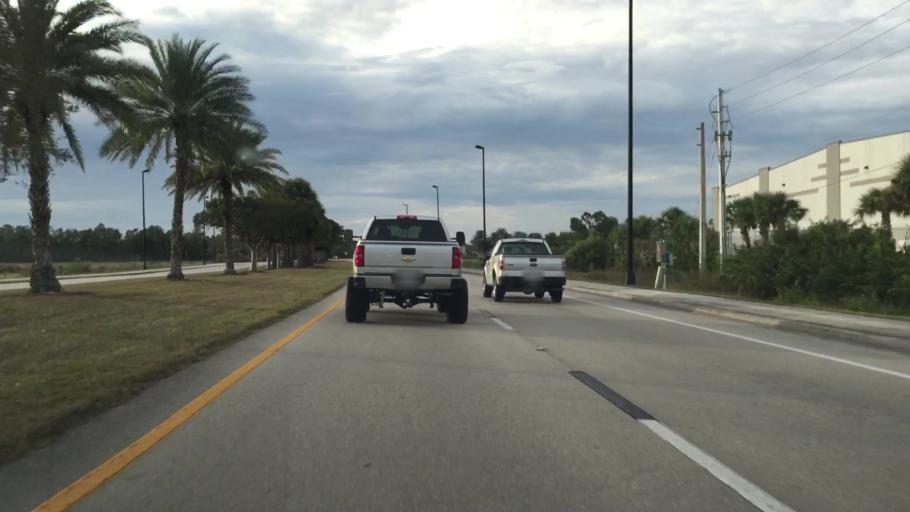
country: US
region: Florida
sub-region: Lee County
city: Gateway
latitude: 26.5399
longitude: -81.7864
